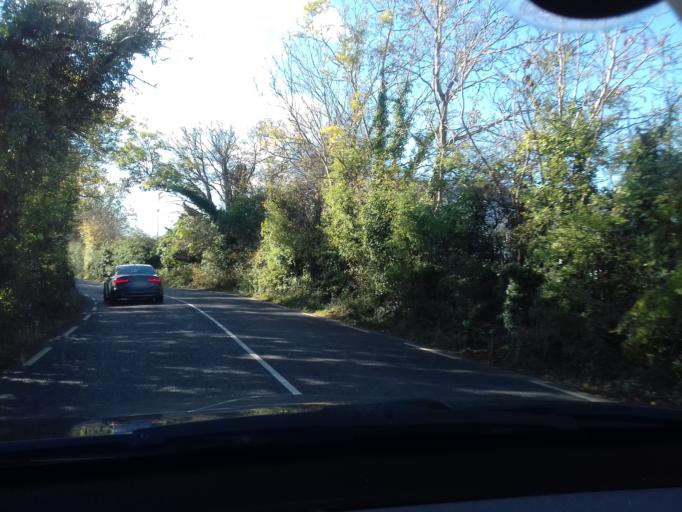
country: IE
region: Leinster
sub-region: Fingal County
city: Blanchardstown
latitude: 53.4205
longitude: -6.3409
